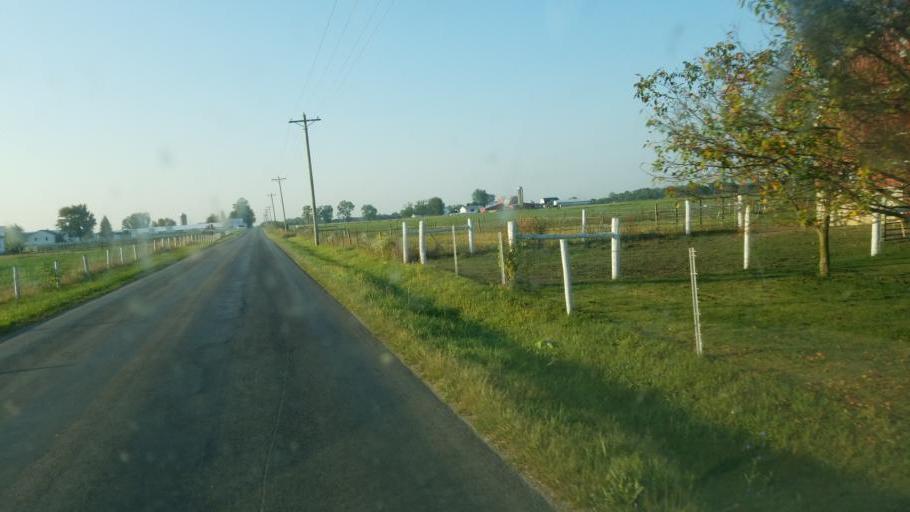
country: US
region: Indiana
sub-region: LaGrange County
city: Lagrange
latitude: 41.6035
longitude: -85.4242
